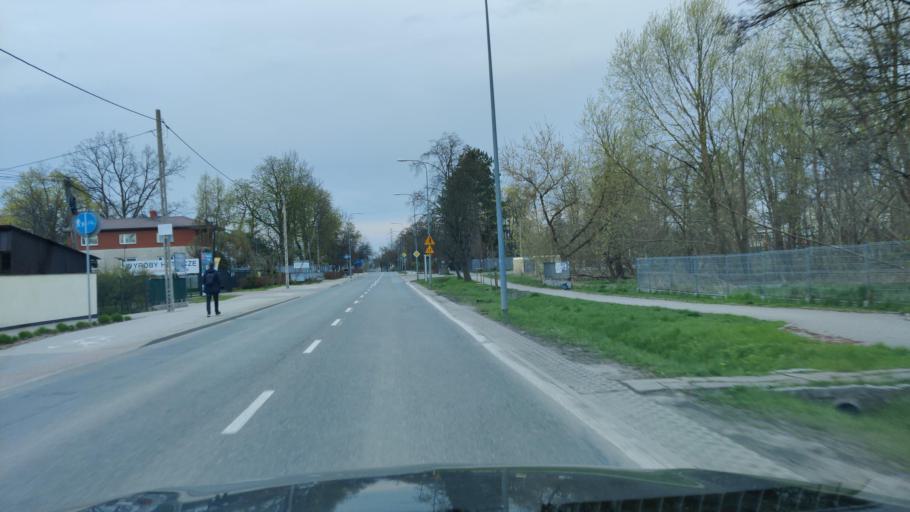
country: PL
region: Masovian Voivodeship
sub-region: Warszawa
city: Kabaty
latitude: 52.1222
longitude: 21.1032
